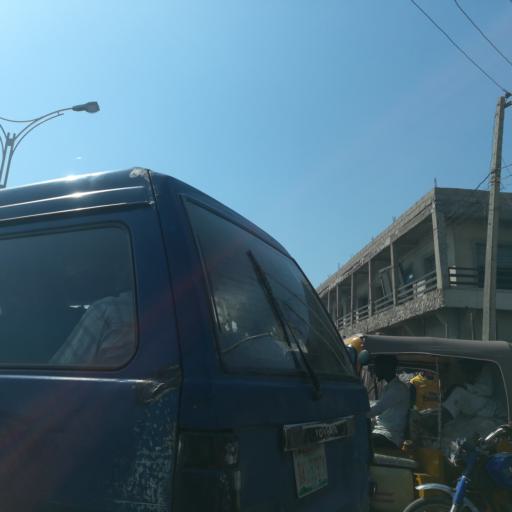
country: NG
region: Kano
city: Kano
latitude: 12.0143
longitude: 8.5344
